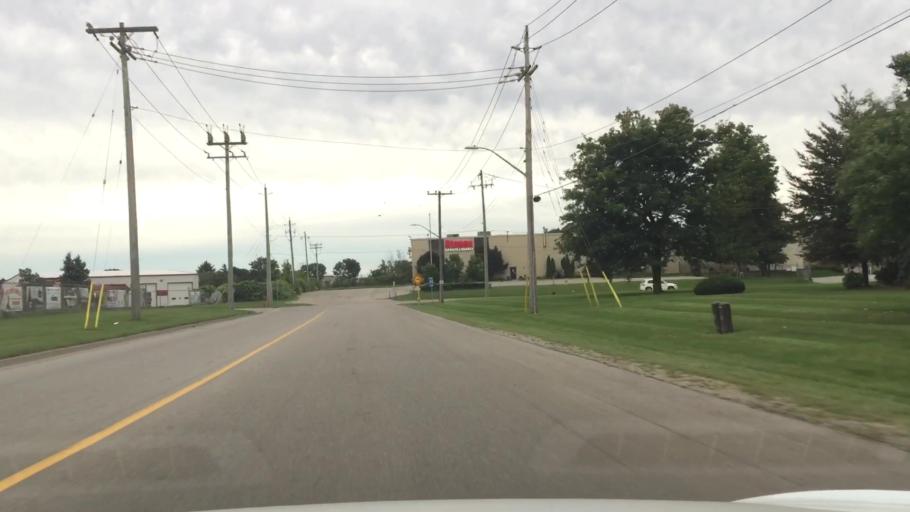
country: CA
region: Ontario
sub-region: Oxford County
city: Woodstock
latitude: 43.1183
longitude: -80.7235
